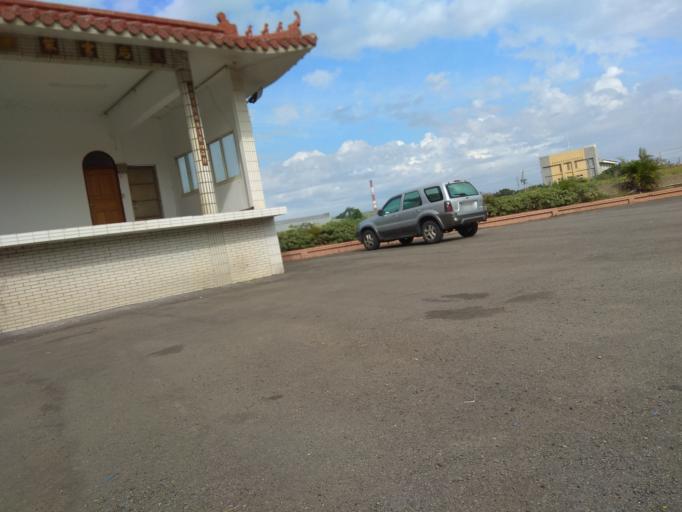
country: TW
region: Taiwan
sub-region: Hsinchu
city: Zhubei
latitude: 24.9759
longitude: 121.0260
